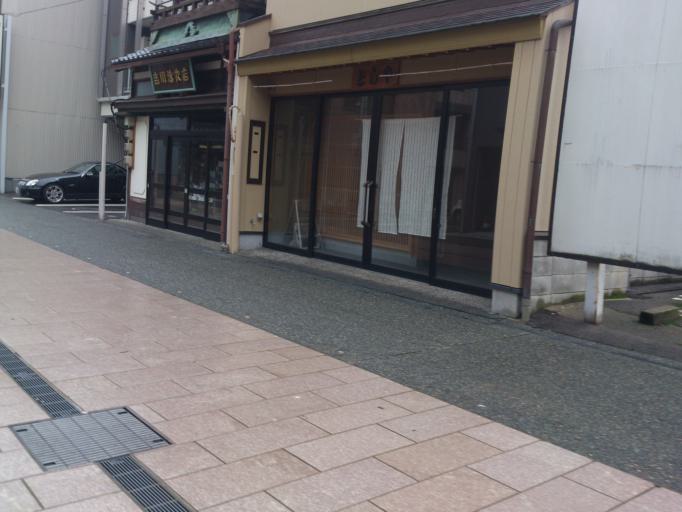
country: JP
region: Ishikawa
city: Kanazawa-shi
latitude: 36.5738
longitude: 136.6555
